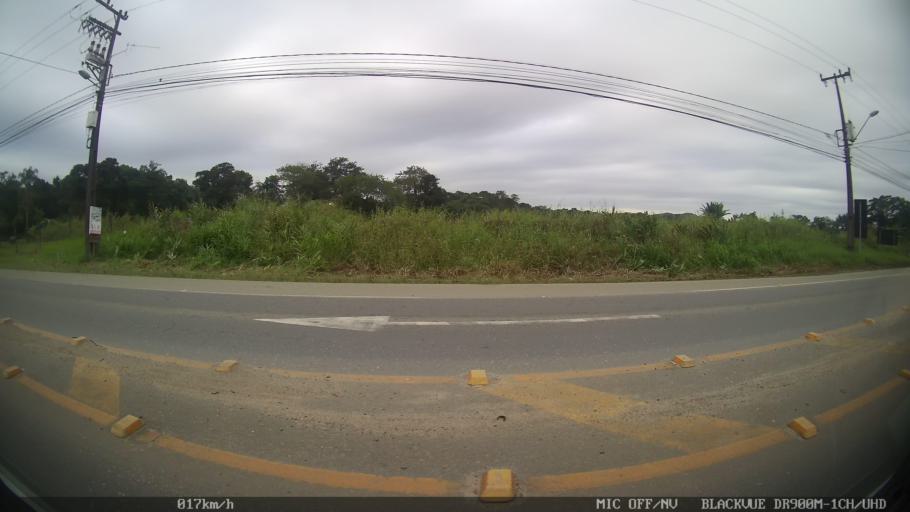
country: BR
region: Santa Catarina
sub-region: Joinville
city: Joinville
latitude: -26.2814
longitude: -48.9235
